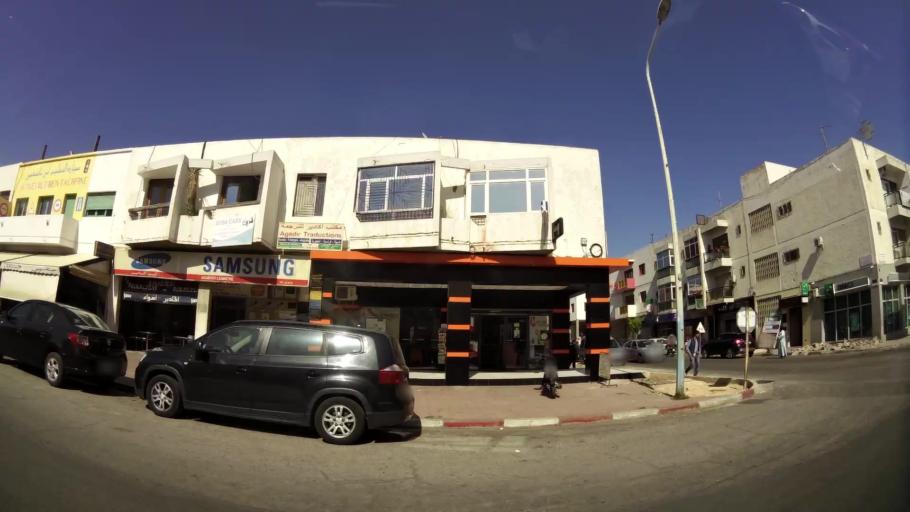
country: MA
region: Souss-Massa-Draa
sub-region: Agadir-Ida-ou-Tnan
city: Agadir
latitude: 30.4162
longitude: -9.5884
